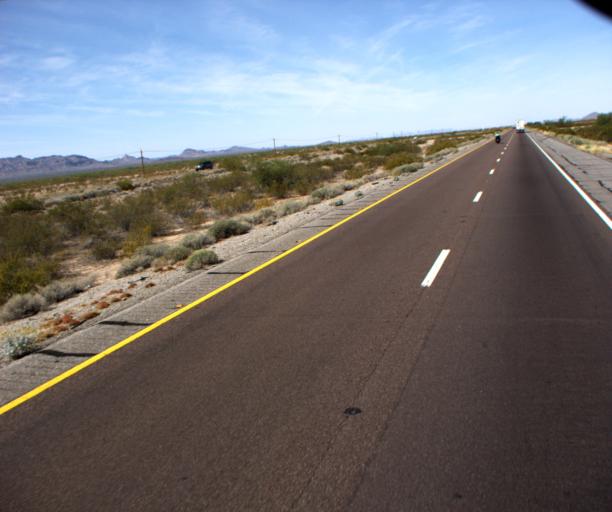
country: US
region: Arizona
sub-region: La Paz County
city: Salome
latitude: 33.5628
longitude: -113.3103
